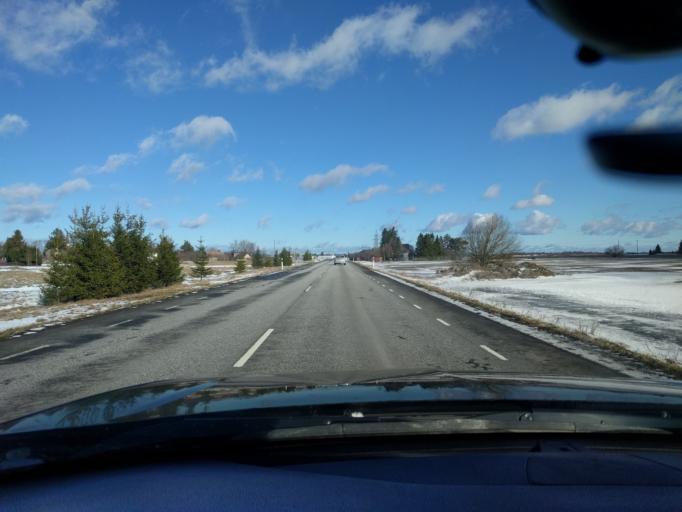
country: EE
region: Harju
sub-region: Raasiku vald
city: Raasiku
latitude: 59.3675
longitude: 25.1907
